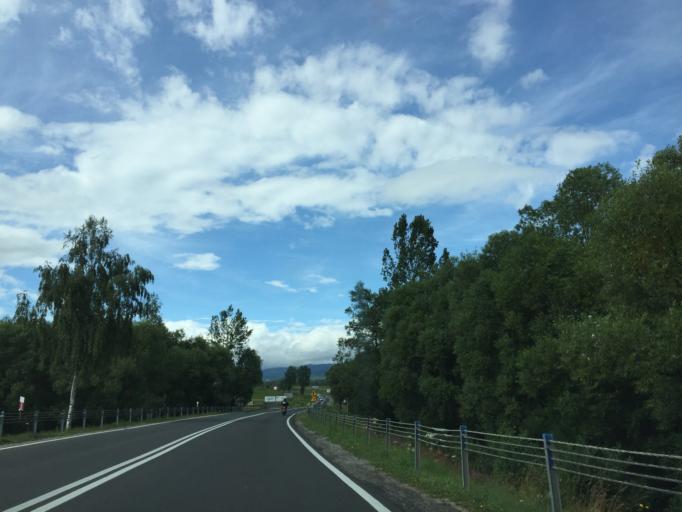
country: PL
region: Lesser Poland Voivodeship
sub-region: Powiat nowotarski
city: Ostrowsko
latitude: 49.4421
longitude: 20.0800
